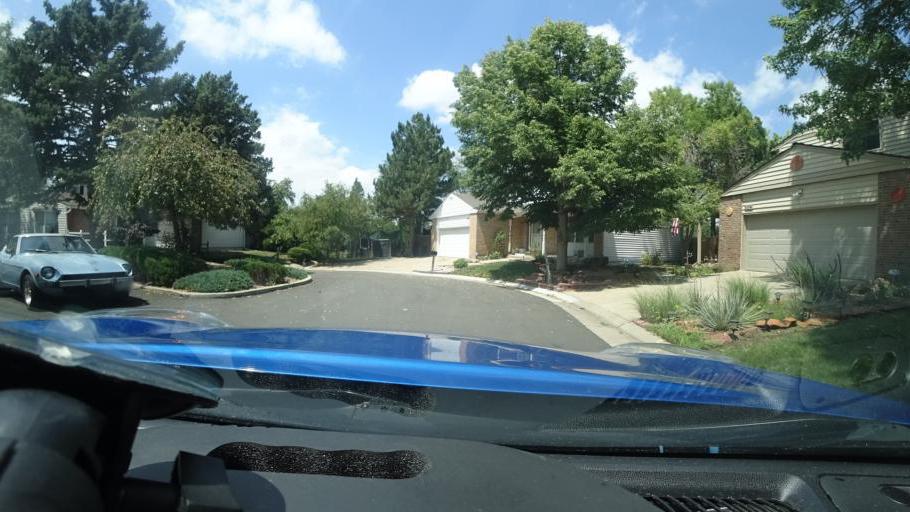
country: US
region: Colorado
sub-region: Adams County
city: Aurora
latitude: 39.7080
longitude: -104.8588
